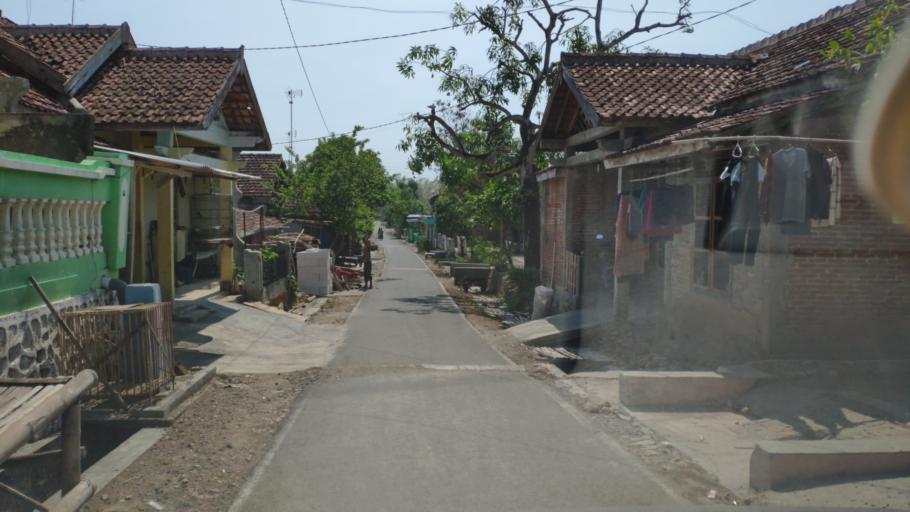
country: ID
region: Central Java
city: Kajangansawan
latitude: -6.9639
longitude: 111.4032
